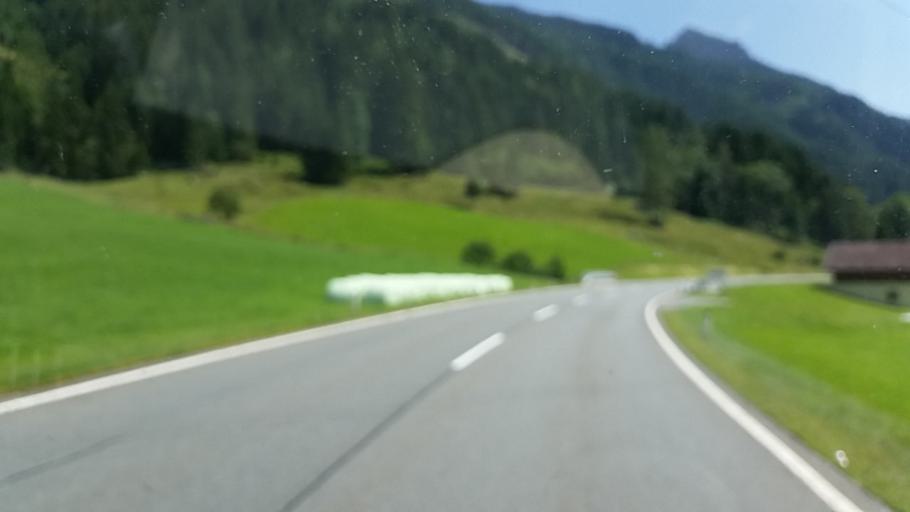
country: AT
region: Salzburg
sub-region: Politischer Bezirk Sankt Johann im Pongau
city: Untertauern
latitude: 47.3352
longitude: 13.5063
